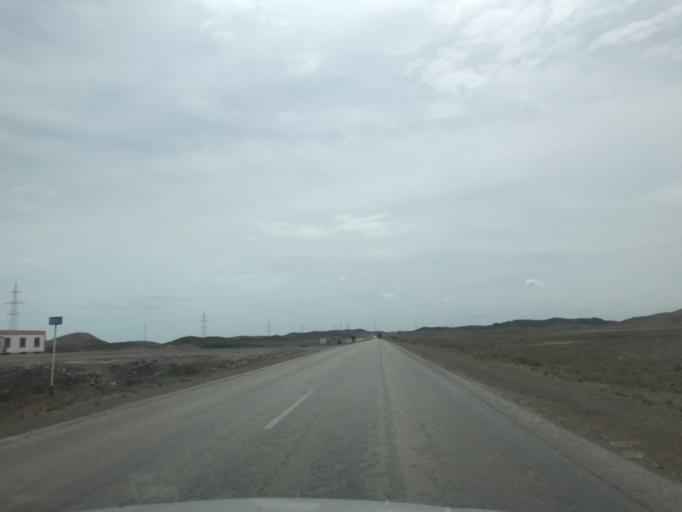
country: KZ
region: Zhambyl
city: Mynaral
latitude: 45.3651
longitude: 73.6657
